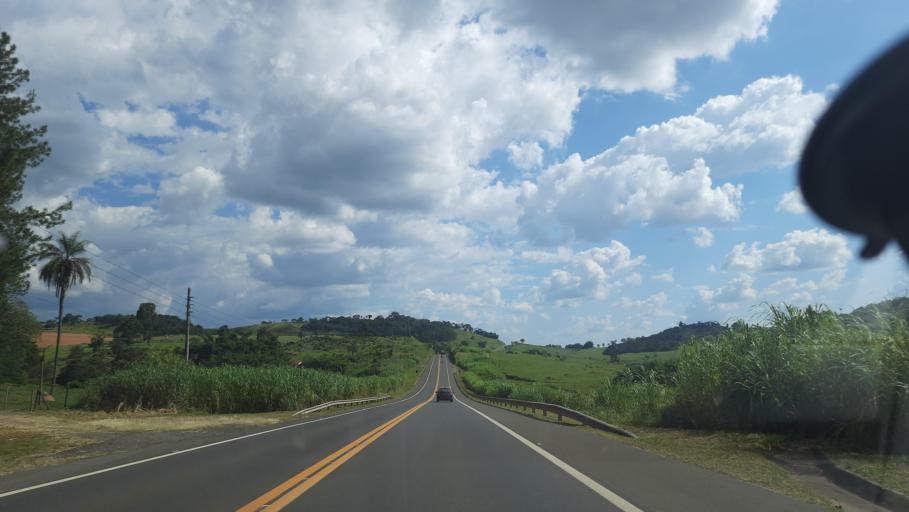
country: BR
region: Sao Paulo
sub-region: Sao Jose Do Rio Pardo
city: Sao Jose do Rio Pardo
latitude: -21.6428
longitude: -46.9070
